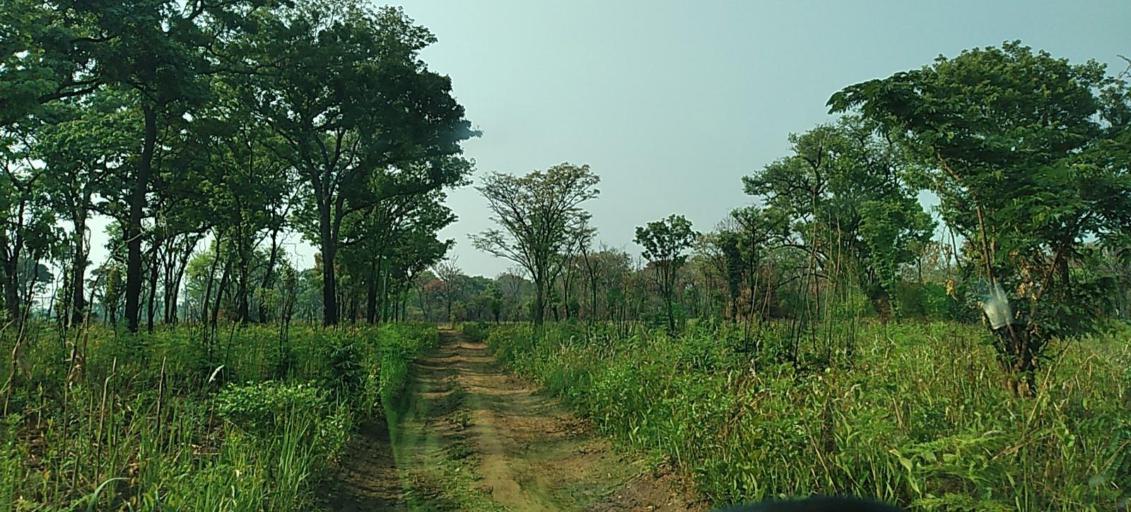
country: ZM
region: North-Western
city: Solwezi
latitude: -12.4042
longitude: 26.5868
